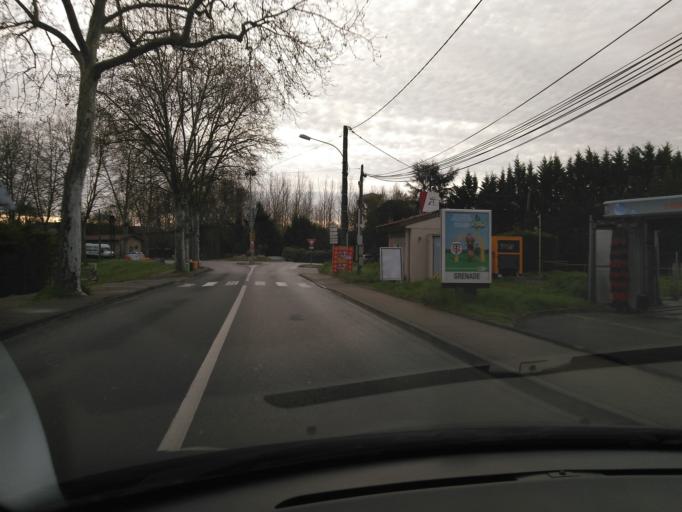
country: FR
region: Midi-Pyrenees
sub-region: Departement de la Haute-Garonne
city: Grenade
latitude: 43.7706
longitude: 1.2861
